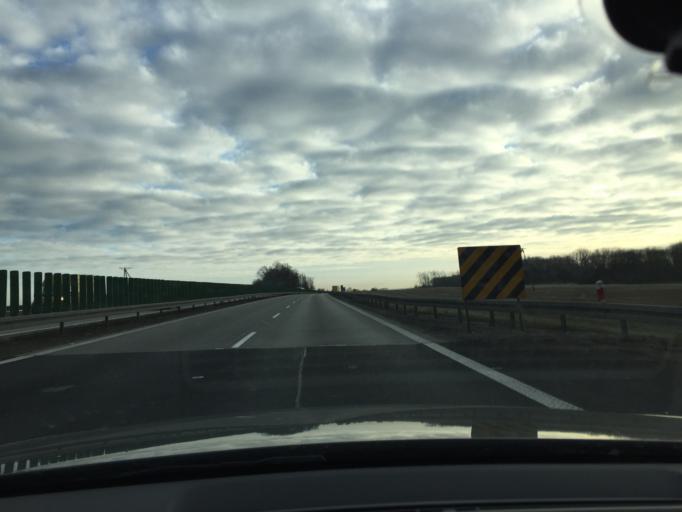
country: PL
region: Lower Silesian Voivodeship
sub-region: Powiat legnicki
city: Legnickie Pole
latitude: 51.1252
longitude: 16.3617
